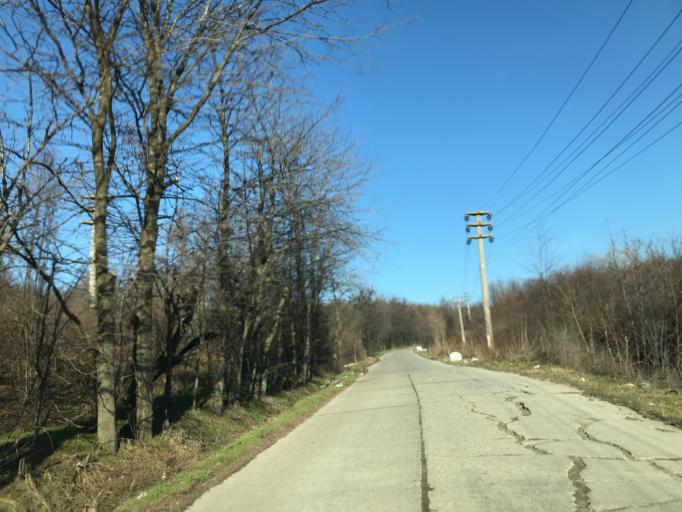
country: RO
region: Olt
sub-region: Municipiul Slatina
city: Slatina
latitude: 44.4101
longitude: 24.3592
